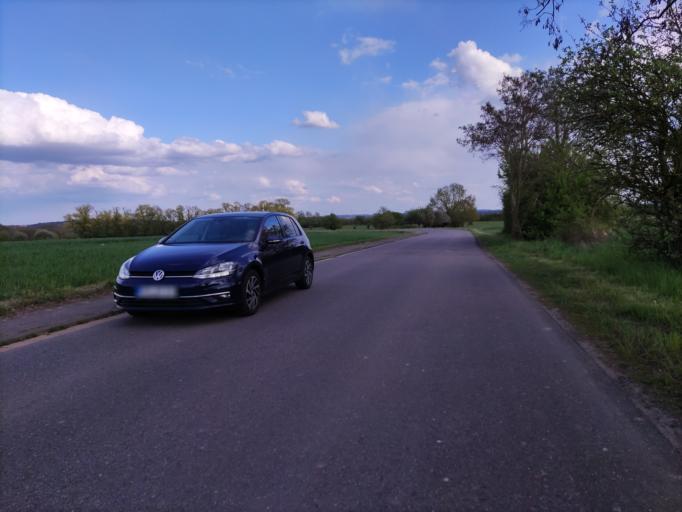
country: DE
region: Saarland
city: Nalbach
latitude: 49.3840
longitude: 6.7673
